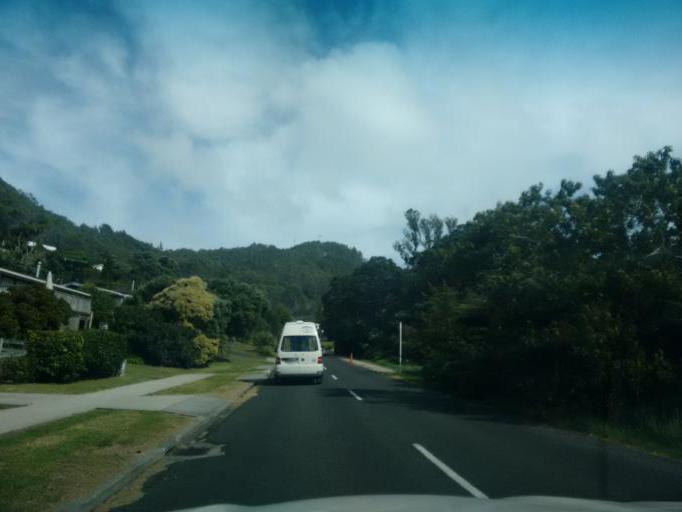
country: NZ
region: Waikato
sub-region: Thames-Coromandel District
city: Whitianga
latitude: -36.8398
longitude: 175.8002
